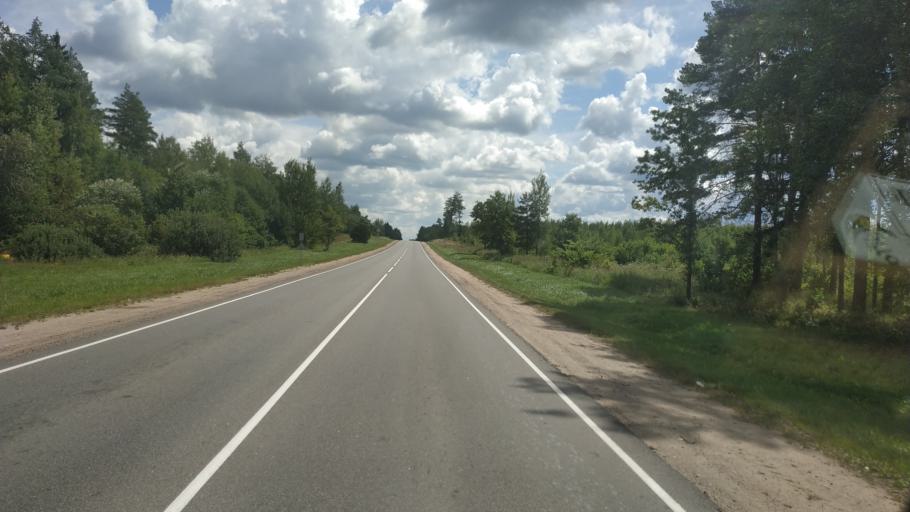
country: BY
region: Mogilev
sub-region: Mahilyowski Rayon
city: Veyno
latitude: 53.8282
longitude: 30.4145
